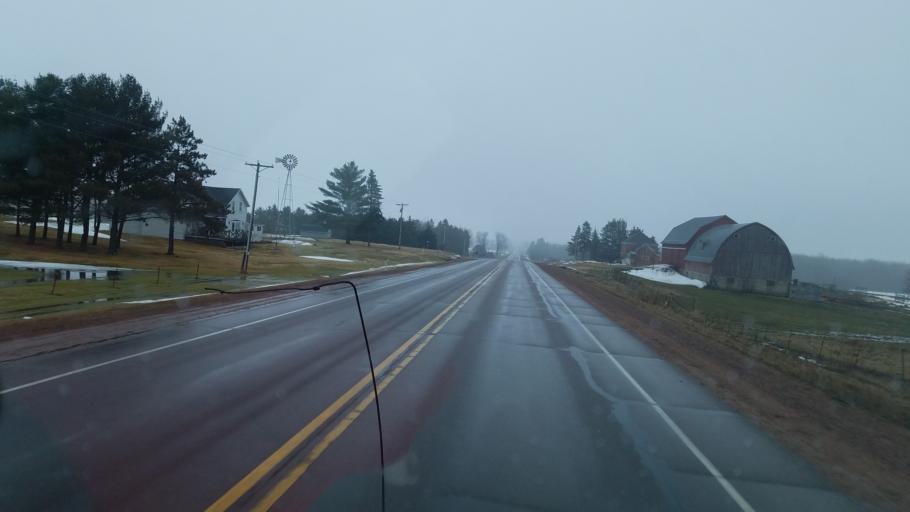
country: US
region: Wisconsin
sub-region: Wood County
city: Marshfield
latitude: 44.5987
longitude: -90.2480
